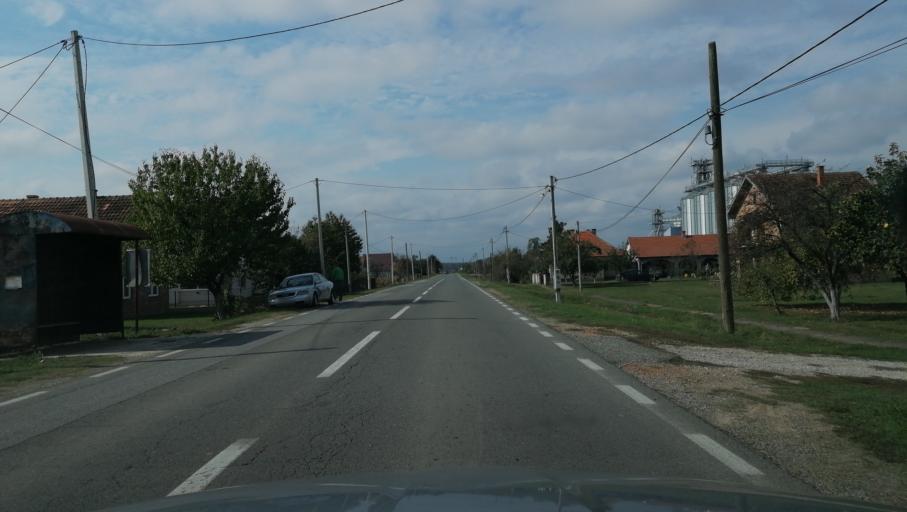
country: RS
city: Bosut
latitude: 44.9244
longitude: 19.3397
